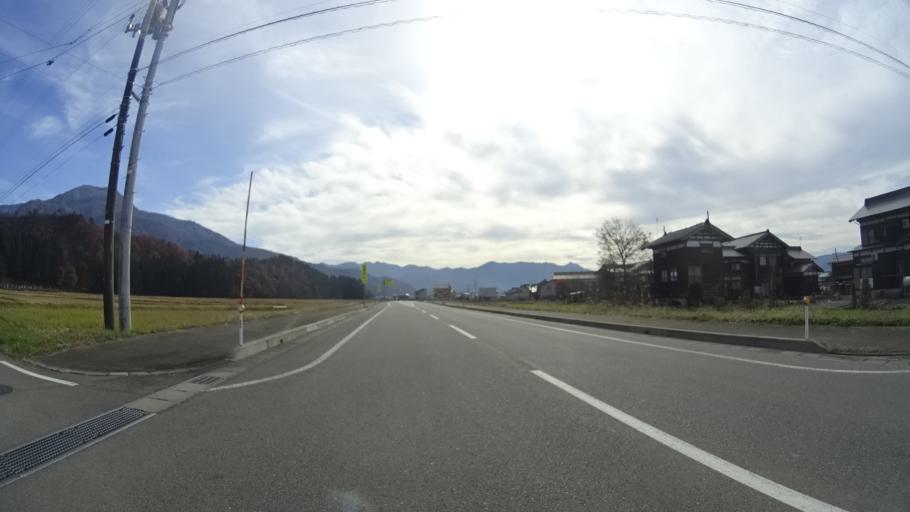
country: JP
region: Niigata
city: Muikamachi
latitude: 37.0534
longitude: 138.8828
